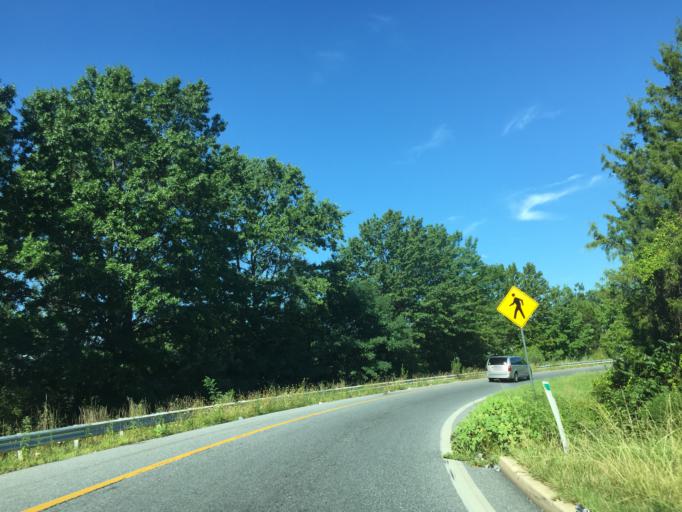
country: US
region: Maryland
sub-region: Baltimore County
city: Essex
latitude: 39.3165
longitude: -76.4576
